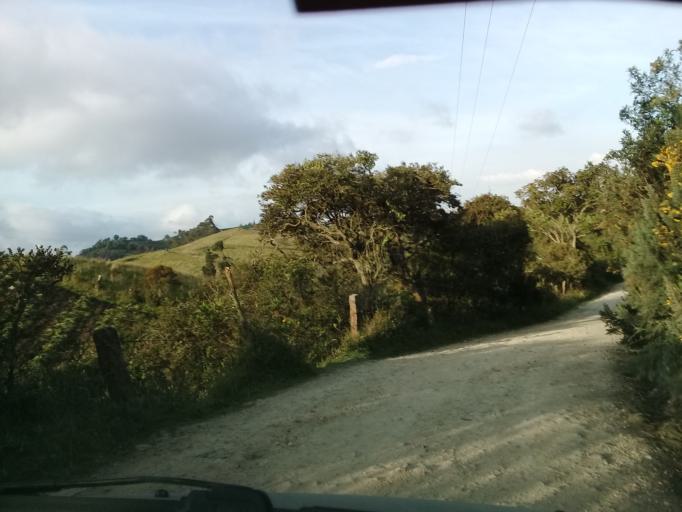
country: CO
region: Cundinamarca
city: Sibate
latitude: 4.4451
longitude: -74.2782
